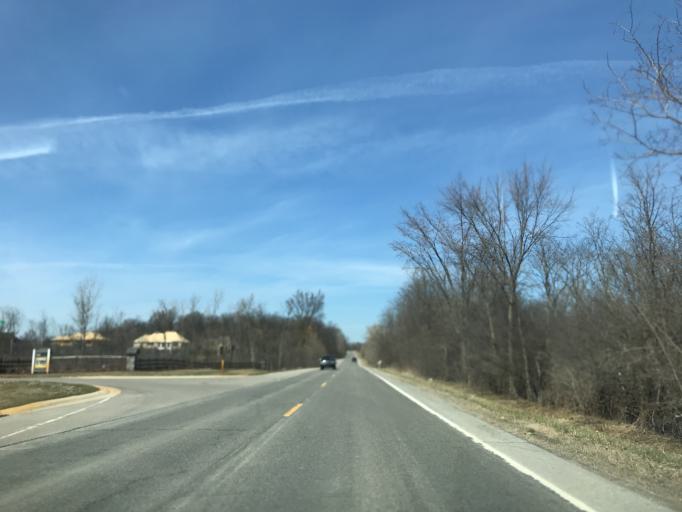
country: US
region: Michigan
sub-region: Washtenaw County
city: Ann Arbor
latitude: 42.3326
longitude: -83.7082
